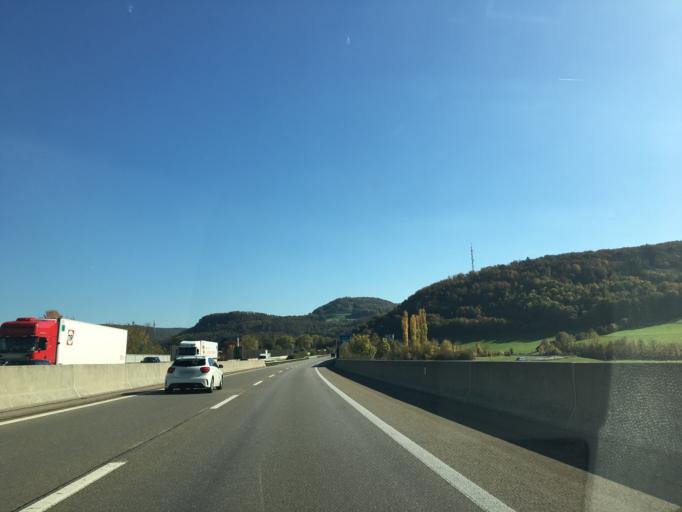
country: CH
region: Basel-Landschaft
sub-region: Bezirk Sissach
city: Itingen
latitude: 47.4695
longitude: 7.7945
